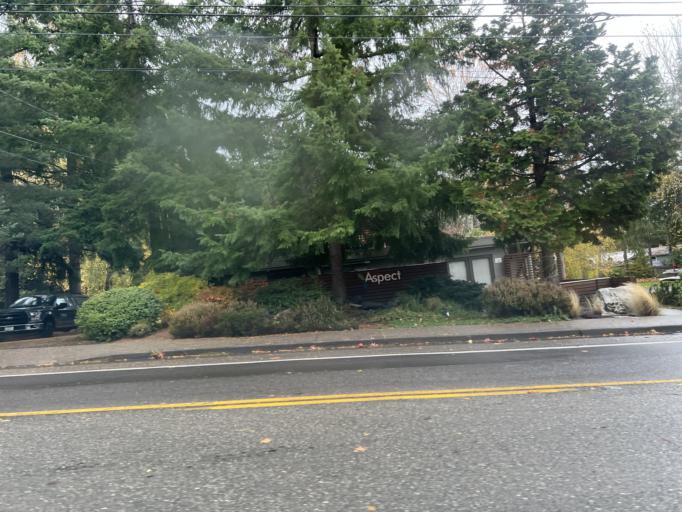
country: US
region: Washington
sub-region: Kitsap County
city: Bainbridge Island
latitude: 47.6273
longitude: -122.5210
